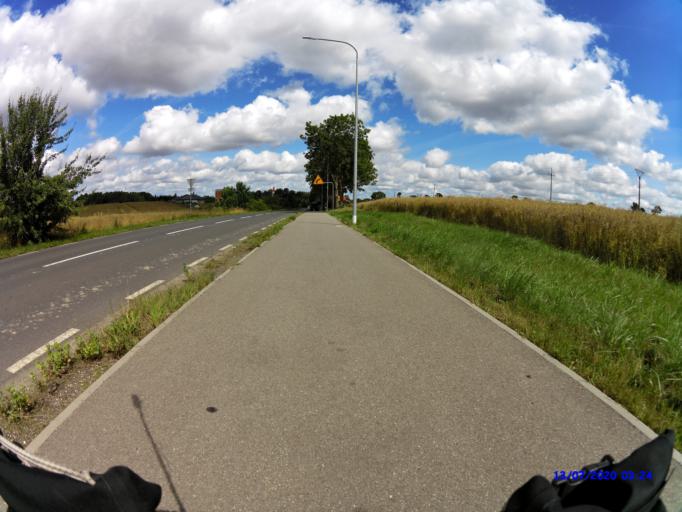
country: PL
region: West Pomeranian Voivodeship
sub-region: Powiat kolobrzeski
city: Goscino
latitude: 54.0423
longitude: 15.6577
